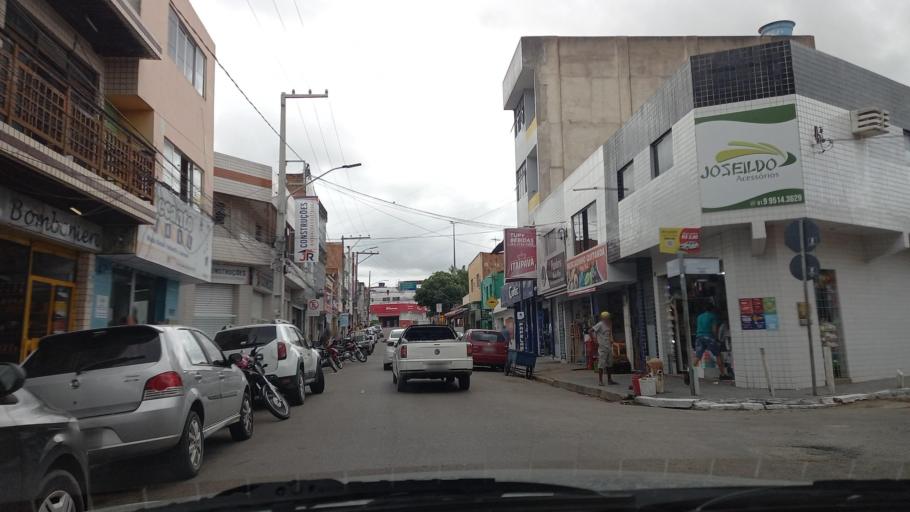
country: BR
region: Pernambuco
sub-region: Caruaru
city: Caruaru
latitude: -8.2793
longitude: -35.9660
